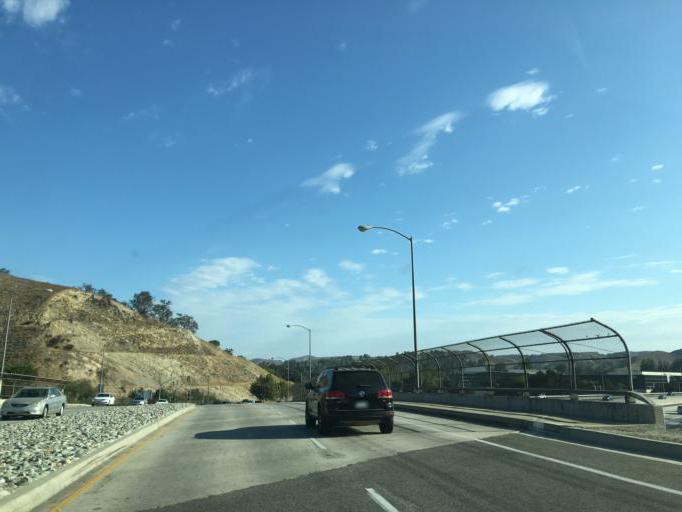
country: US
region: California
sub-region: Los Angeles County
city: Agoura
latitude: 34.1481
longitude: -118.6977
